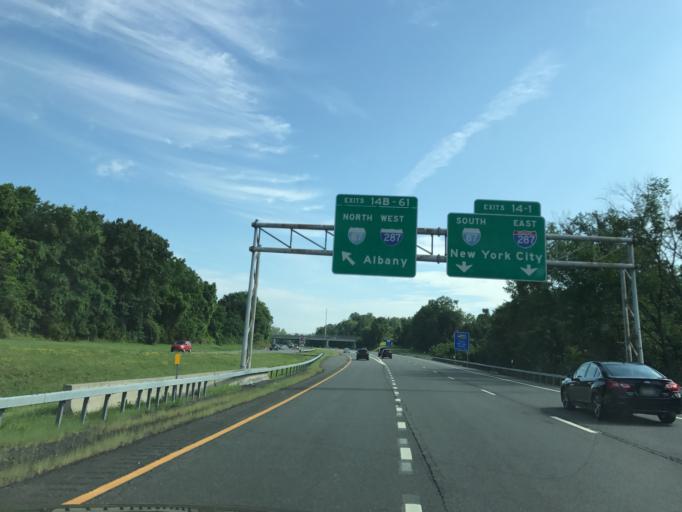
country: US
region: New York
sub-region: Rockland County
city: Chestnut Ridge
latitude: 41.0885
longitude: -74.0414
